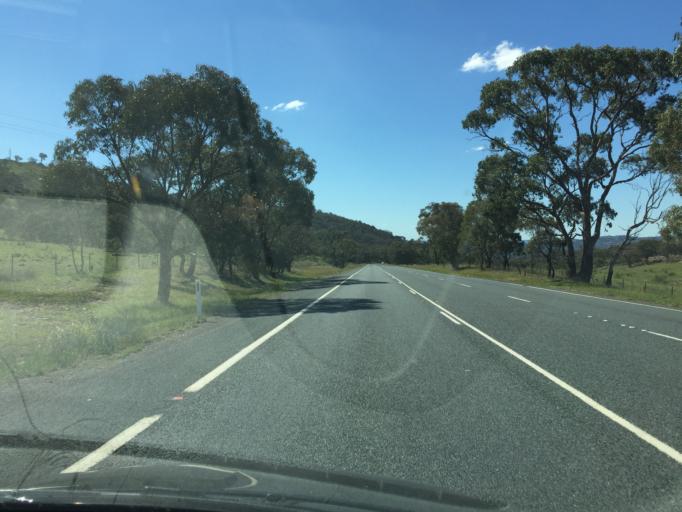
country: AU
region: Australian Capital Territory
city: Macarthur
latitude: -35.4737
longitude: 149.1409
